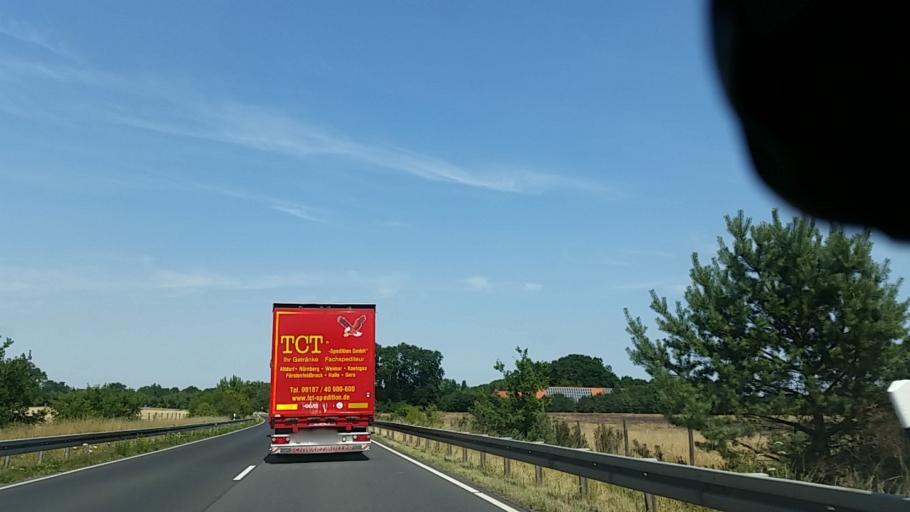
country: DE
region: Lower Saxony
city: Wietzen
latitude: 52.6728
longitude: 9.1058
